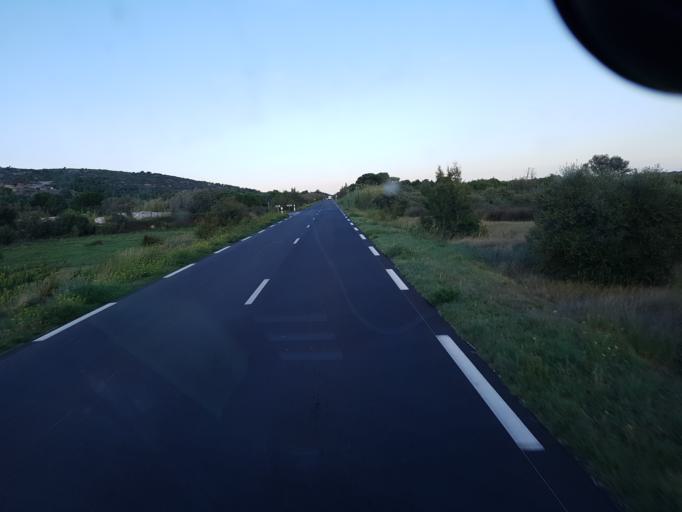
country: FR
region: Languedoc-Roussillon
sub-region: Departement de l'Aude
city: Port-la-Nouvelle
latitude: 42.9787
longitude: 3.0145
